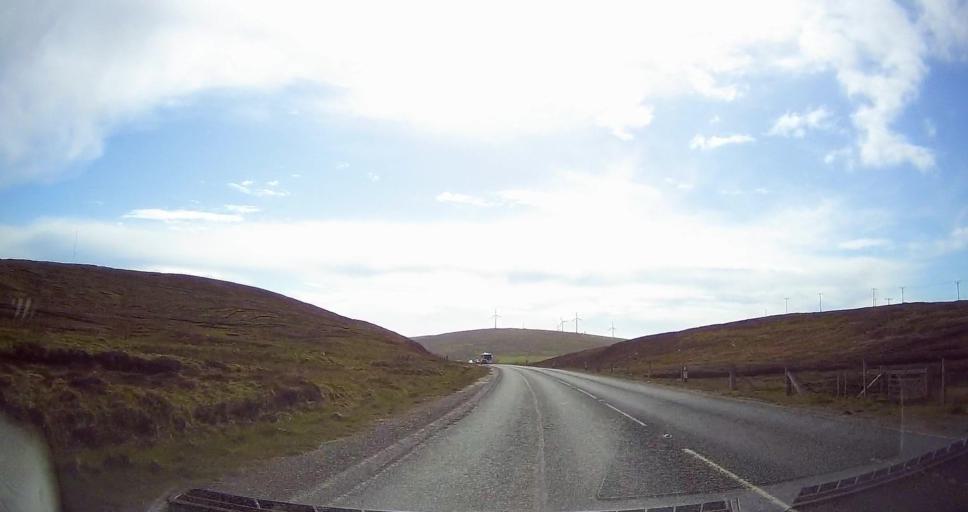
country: GB
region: Scotland
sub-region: Shetland Islands
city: Lerwick
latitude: 60.1675
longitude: -1.1998
